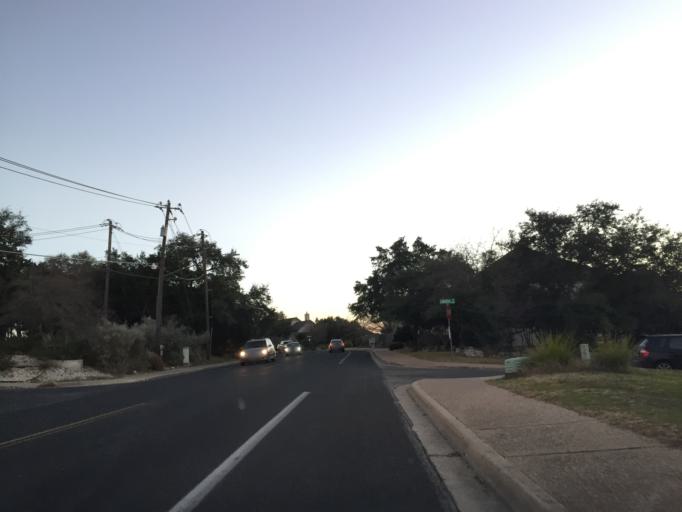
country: US
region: Texas
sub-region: Williamson County
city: Jollyville
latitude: 30.4001
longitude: -97.7677
